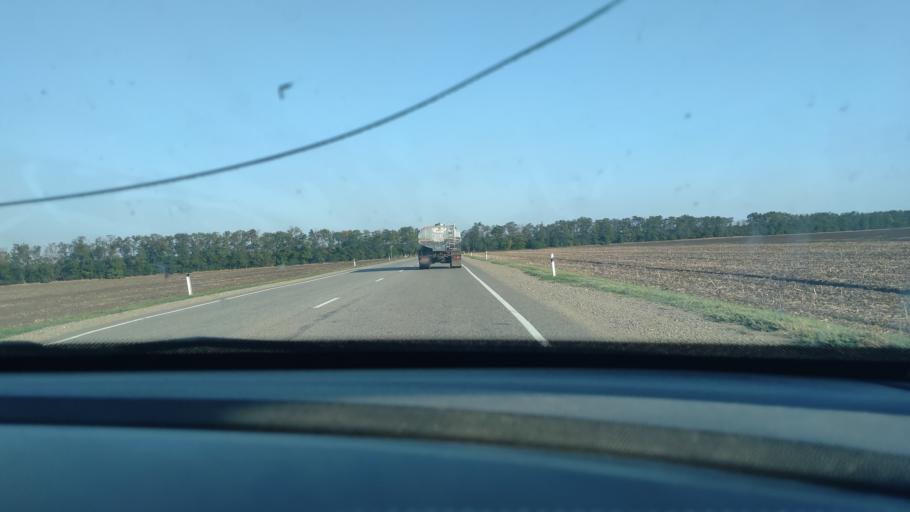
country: RU
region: Krasnodarskiy
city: Starominskaya
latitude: 46.5017
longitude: 39.0438
